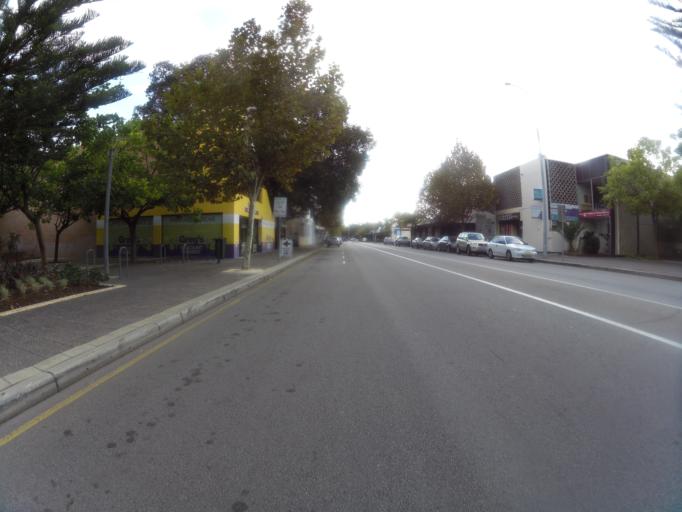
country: AU
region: Western Australia
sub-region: Fremantle
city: Fremantle
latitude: -32.0530
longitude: 115.7511
